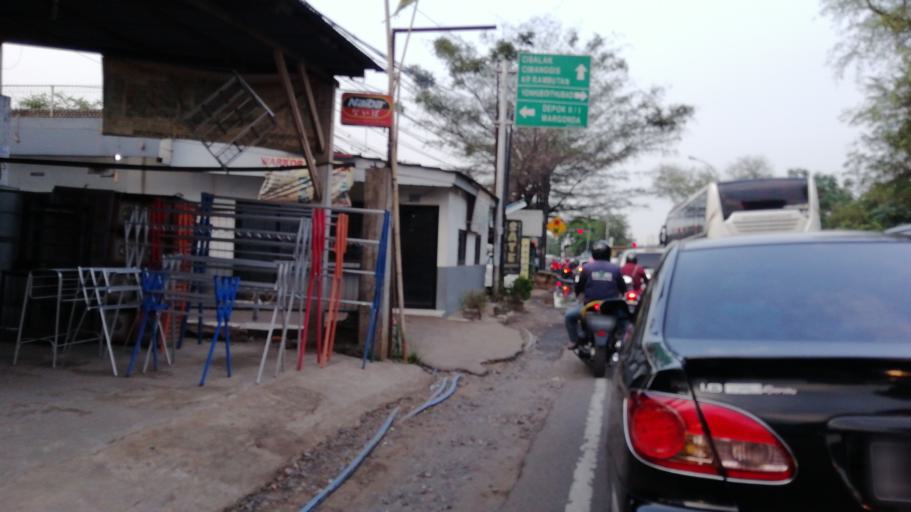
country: ID
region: West Java
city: Depok
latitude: -6.4116
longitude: 106.8610
